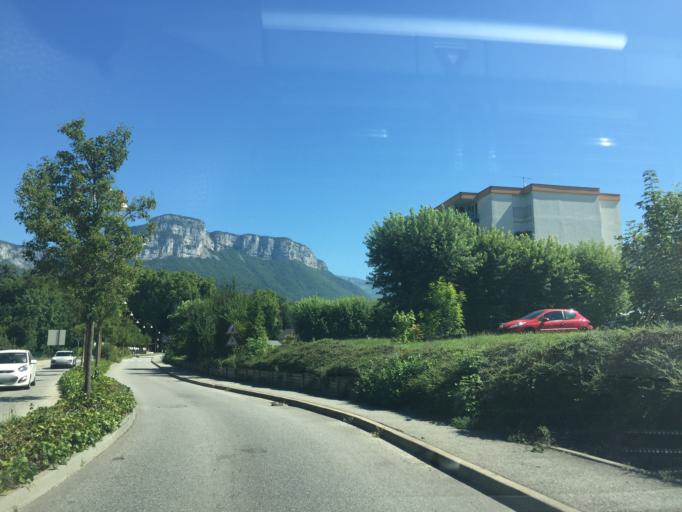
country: FR
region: Rhone-Alpes
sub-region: Departement de la Savoie
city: La Ravoire
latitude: 45.5605
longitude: 5.9603
